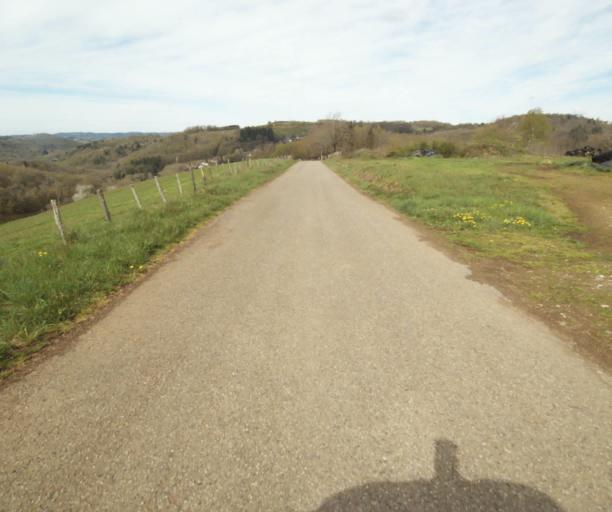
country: FR
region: Limousin
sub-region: Departement de la Correze
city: Laguenne
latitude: 45.2501
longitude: 1.8317
